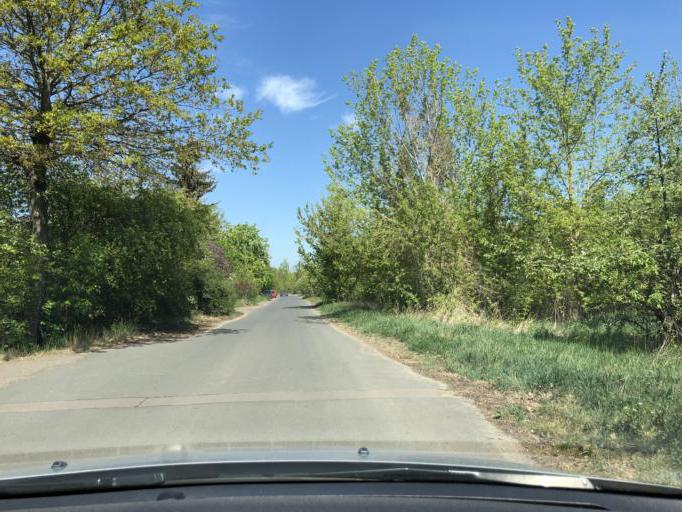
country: DE
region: Saxony-Anhalt
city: Dieskau
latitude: 51.4485
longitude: 11.9991
